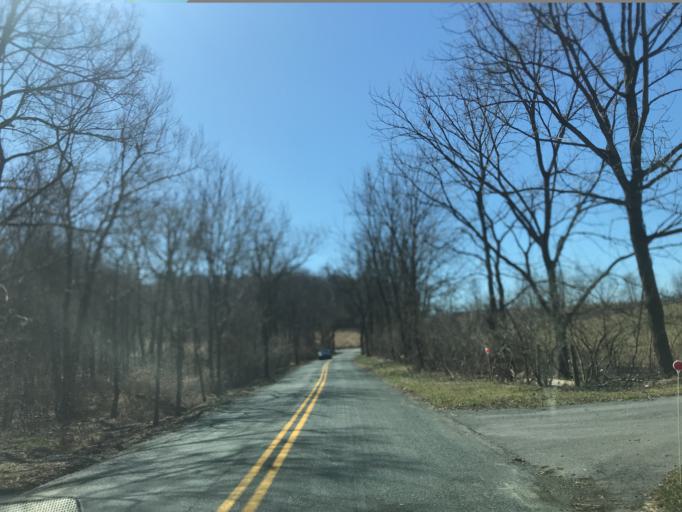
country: US
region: Pennsylvania
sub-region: York County
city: Stewartstown
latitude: 39.7052
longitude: -76.5199
